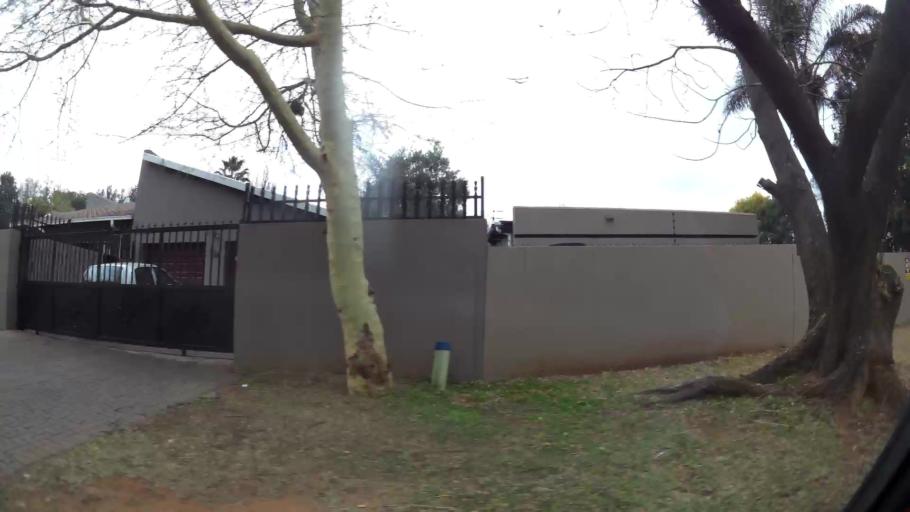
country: ZA
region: Gauteng
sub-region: City of Johannesburg Metropolitan Municipality
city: Roodepoort
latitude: -26.1211
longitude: 27.9054
